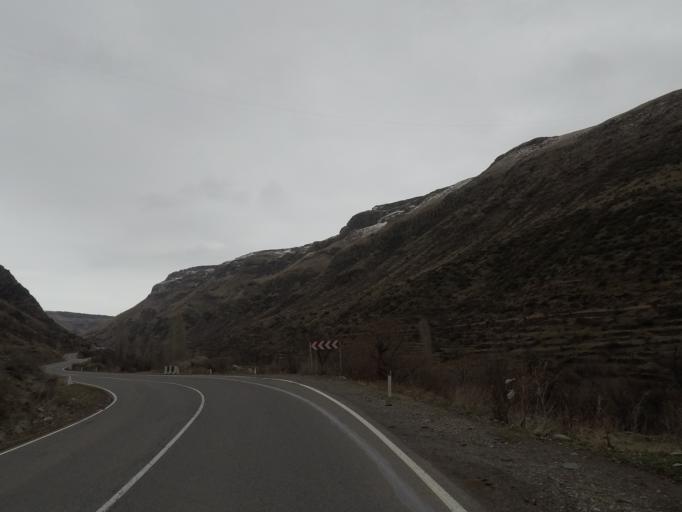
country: GE
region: Samtskhe-Javakheti
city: Aspindza
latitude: 41.4816
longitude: 43.2885
